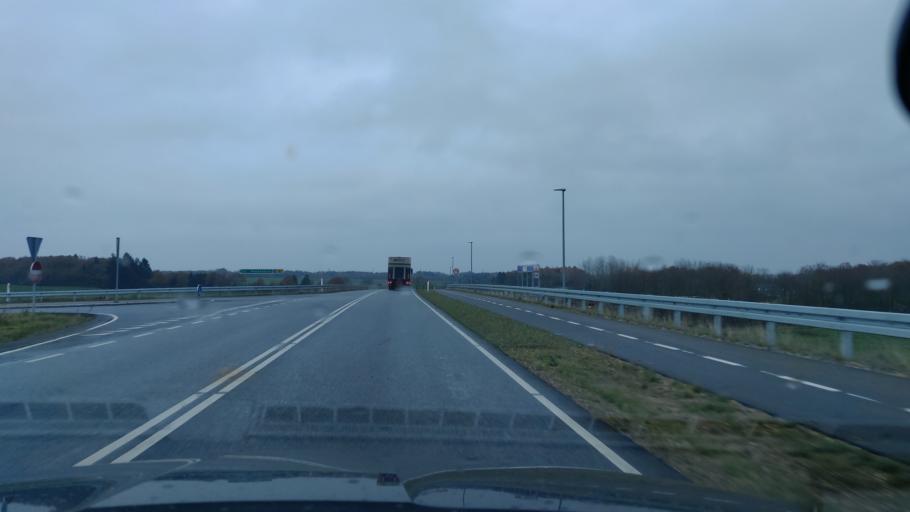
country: DK
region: Central Jutland
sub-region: Herning Kommune
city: Avlum
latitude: 56.2195
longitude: 8.8508
